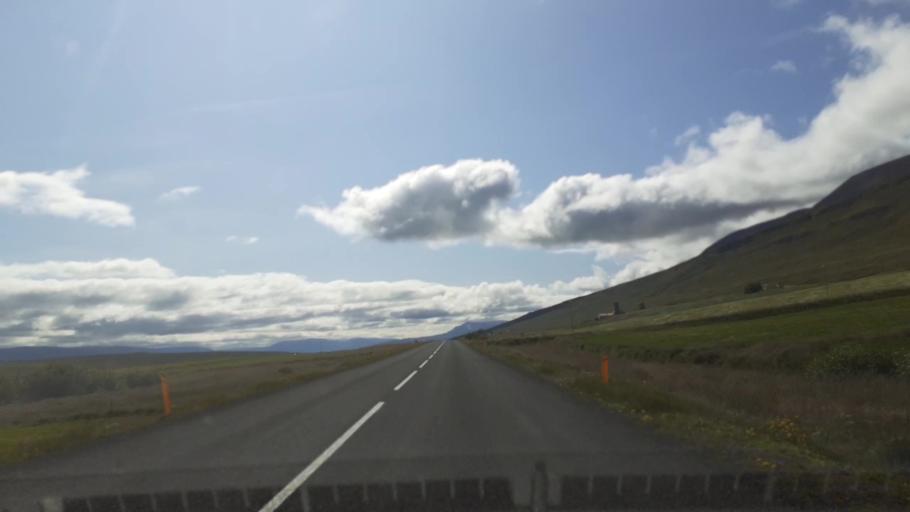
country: IS
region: Northeast
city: Akureyri
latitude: 65.8633
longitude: -18.2612
